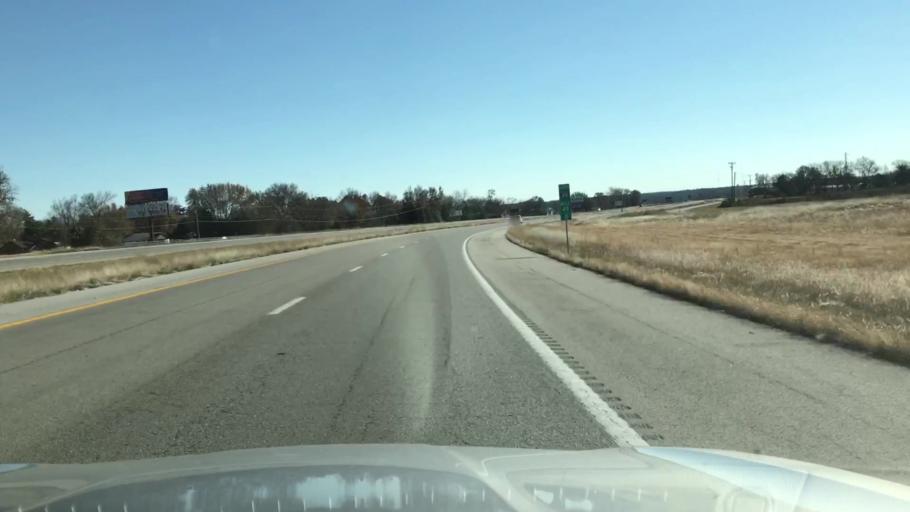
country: US
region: Missouri
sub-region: Jasper County
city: Carthage
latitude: 37.1304
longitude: -94.3117
